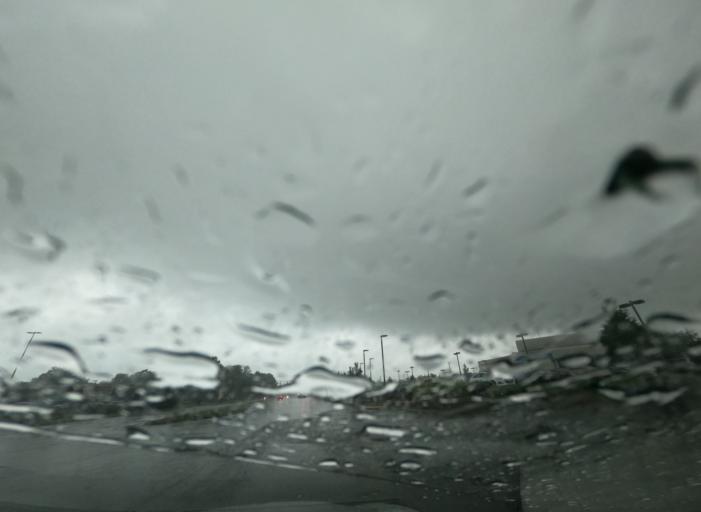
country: US
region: Kentucky
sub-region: Jefferson County
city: Hurstbourne Acres
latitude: 38.2178
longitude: -85.5831
